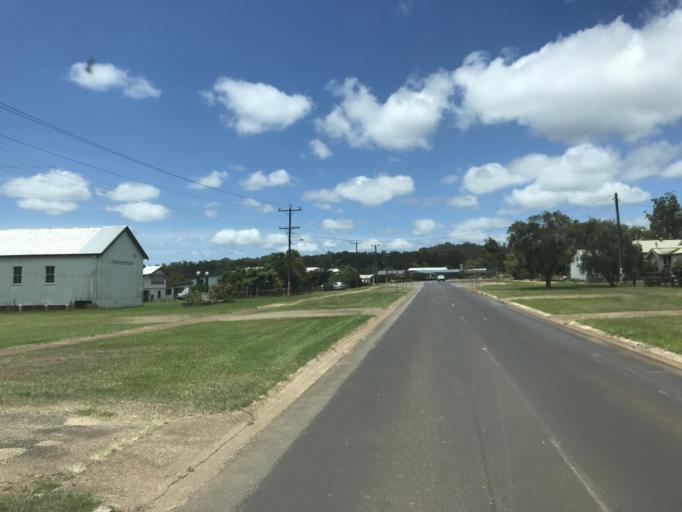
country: AU
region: Queensland
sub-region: Tablelands
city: Ravenshoe
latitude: -17.6122
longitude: 145.4869
